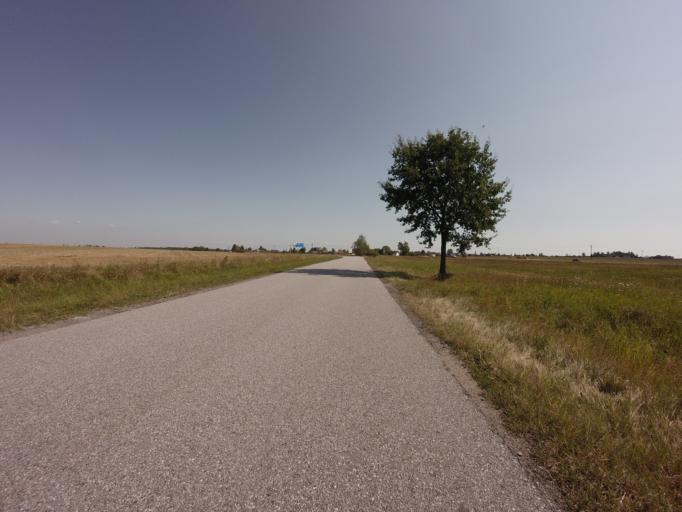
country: CZ
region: Jihocesky
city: Kamenny Ujezd
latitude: 48.8931
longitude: 14.4355
